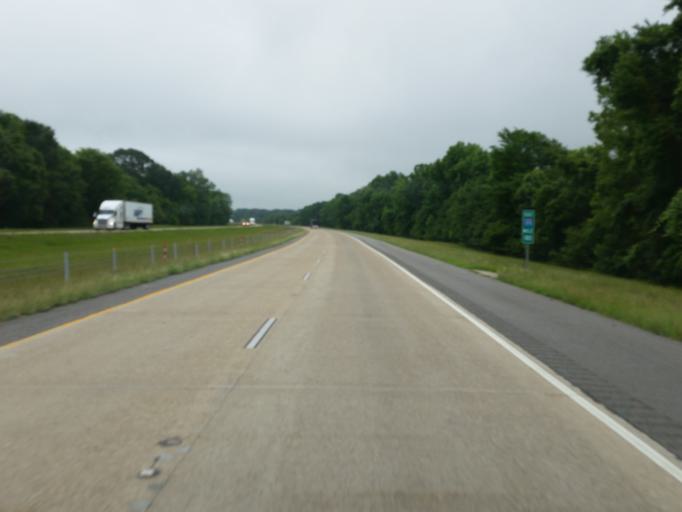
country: US
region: Louisiana
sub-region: Madison Parish
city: Tallulah
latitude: 32.3376
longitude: -91.0652
